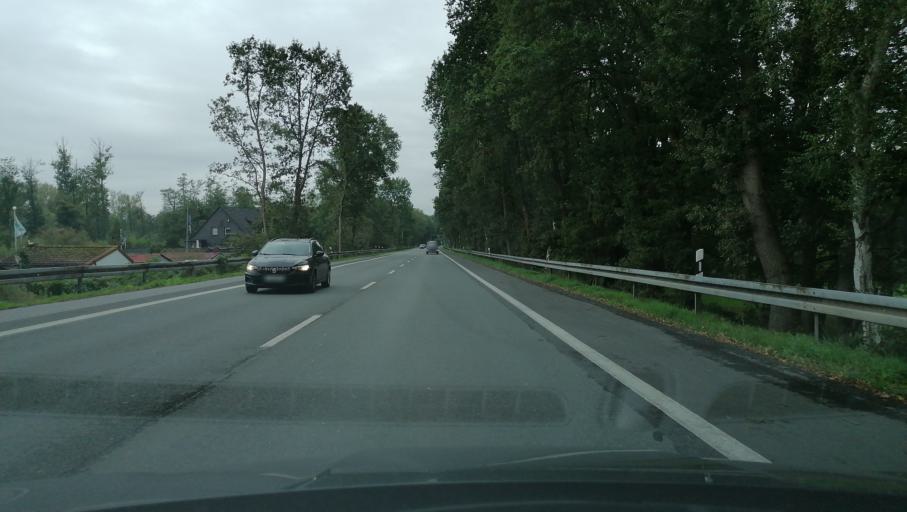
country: DE
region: North Rhine-Westphalia
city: Herten
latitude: 51.5627
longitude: 7.1217
